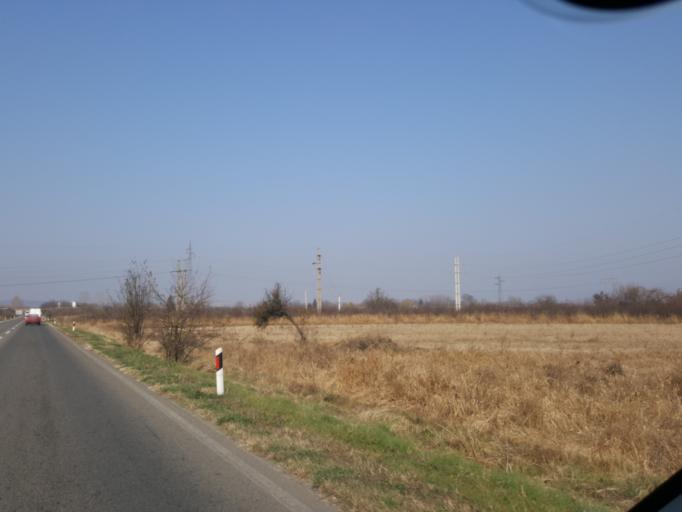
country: RS
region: Central Serbia
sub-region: Jablanicki Okrug
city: Leskovac
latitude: 43.0143
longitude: 21.9566
